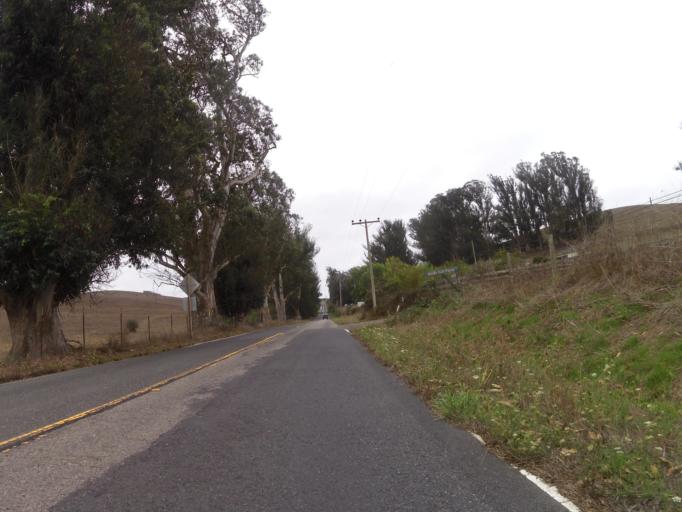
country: US
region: California
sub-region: Sonoma County
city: Occidental
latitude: 38.3039
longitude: -122.8968
